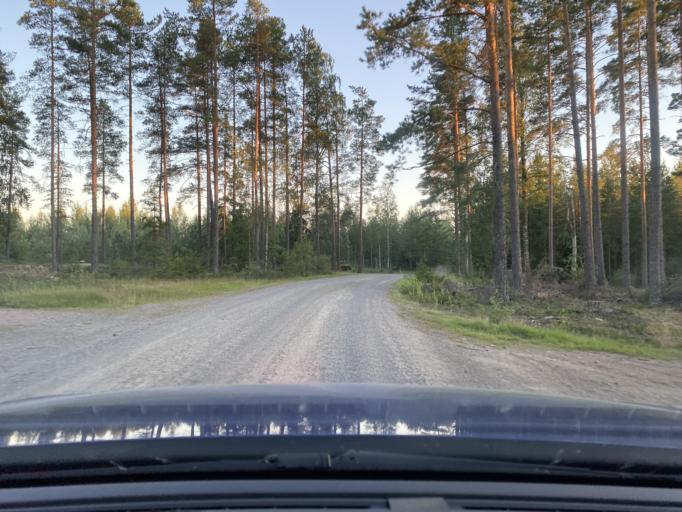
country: FI
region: Satakunta
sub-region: Rauma
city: Kiukainen
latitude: 61.1375
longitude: 22.0236
